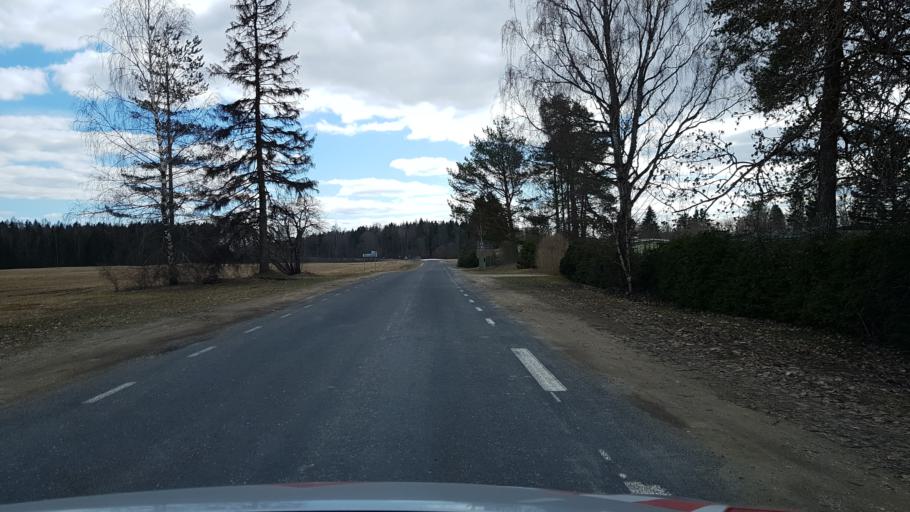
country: EE
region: Laeaene-Virumaa
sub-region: Kadrina vald
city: Kadrina
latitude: 59.2527
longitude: 26.2195
